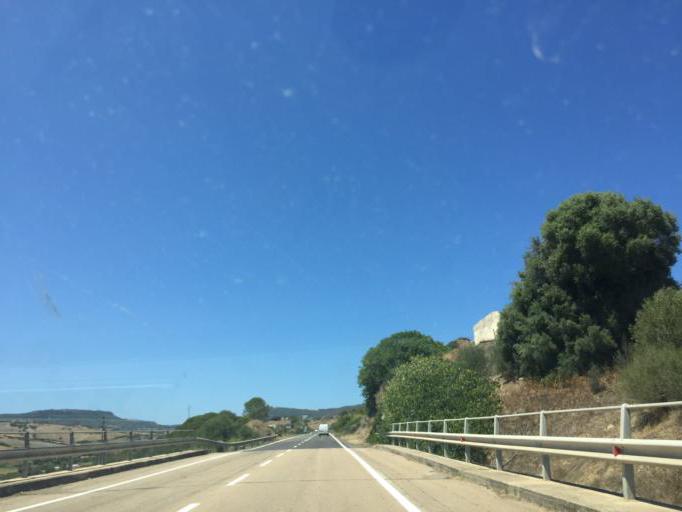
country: IT
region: Sardinia
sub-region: Provincia di Sassari
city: Valledoria
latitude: 40.9061
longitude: 8.8045
